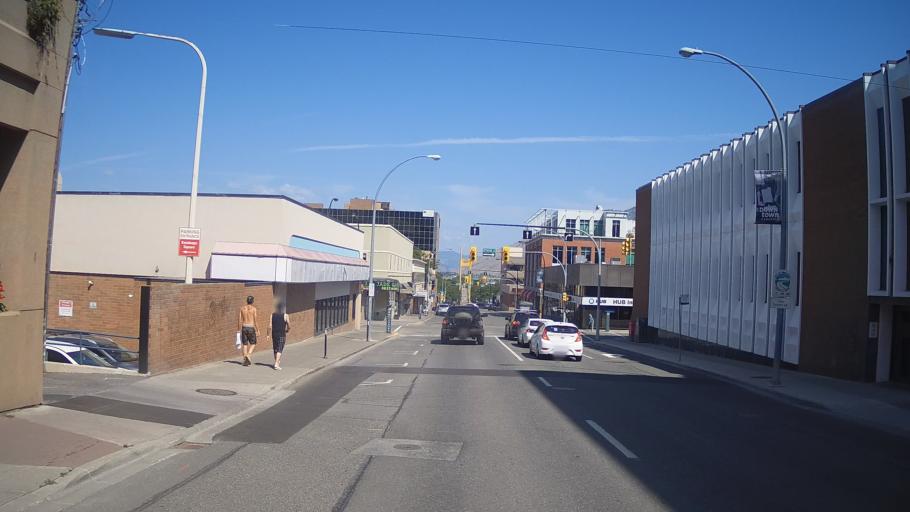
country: CA
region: British Columbia
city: Kamloops
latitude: 50.6743
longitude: -120.3345
